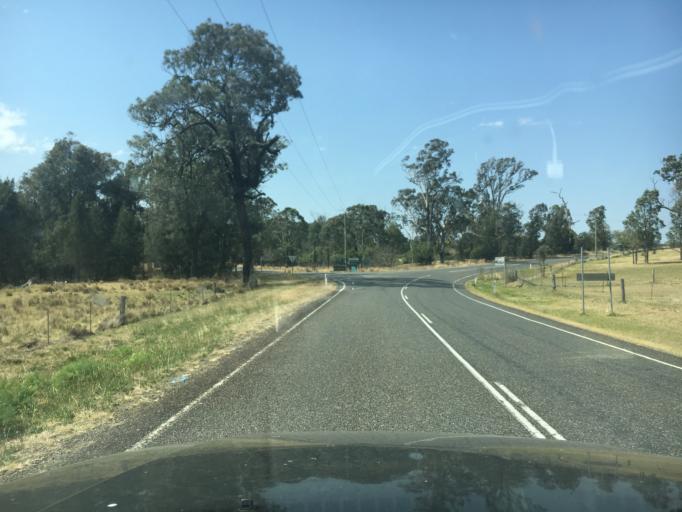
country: AU
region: New South Wales
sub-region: Singleton
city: Singleton
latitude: -32.5444
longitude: 151.2442
